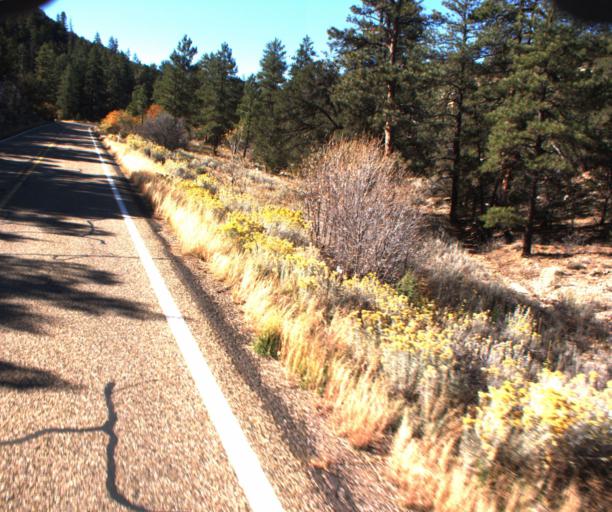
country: US
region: Arizona
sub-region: Coconino County
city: Fredonia
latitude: 36.7405
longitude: -112.1249
